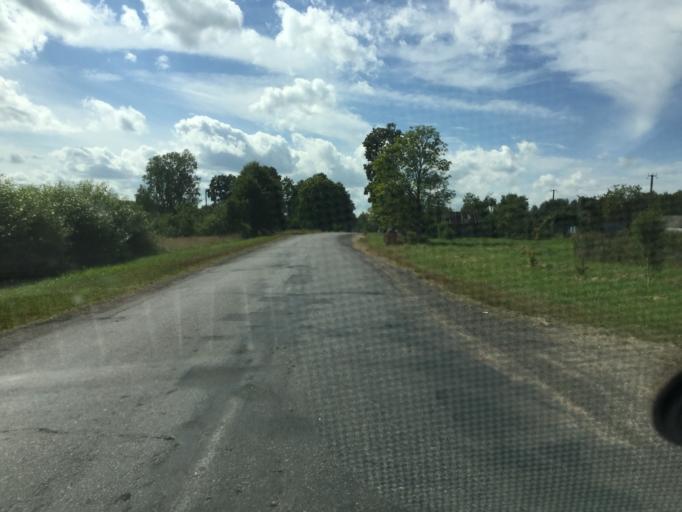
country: BY
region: Vitebsk
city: Chashniki
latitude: 55.2844
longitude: 29.3537
